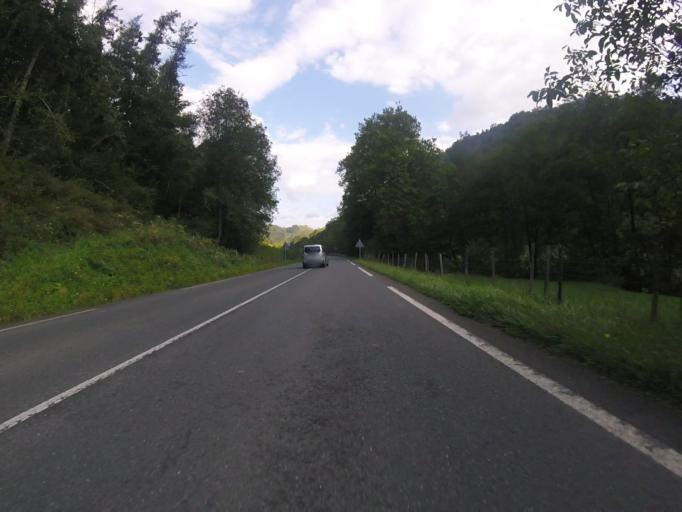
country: ES
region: Basque Country
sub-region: Provincia de Guipuzcoa
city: Amezqueta
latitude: 43.0702
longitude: -2.0844
